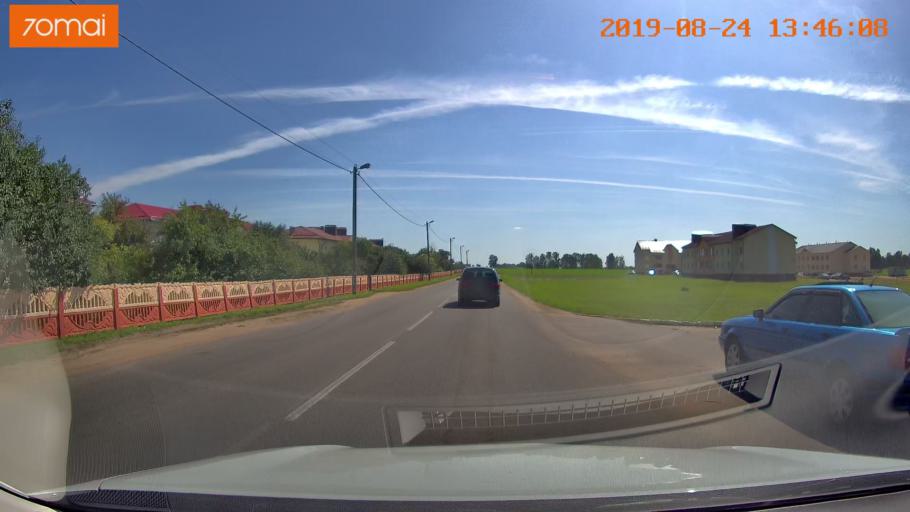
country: BY
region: Minsk
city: Samakhvalavichy
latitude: 53.6760
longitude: 27.5310
